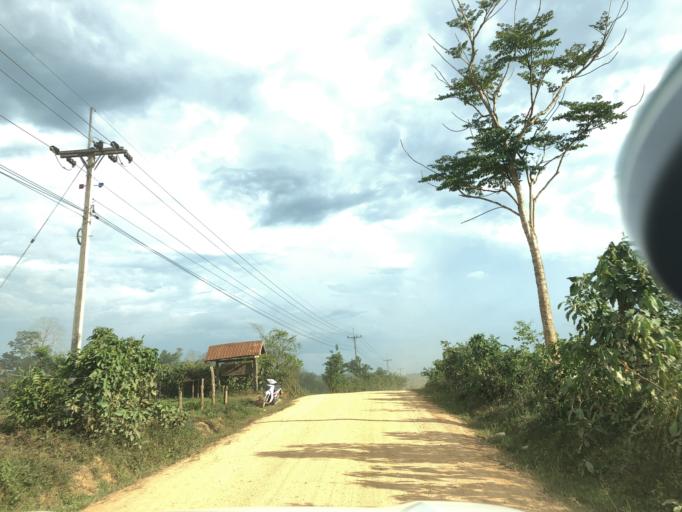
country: TH
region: Loei
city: Chiang Khan
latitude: 18.0111
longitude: 101.4203
